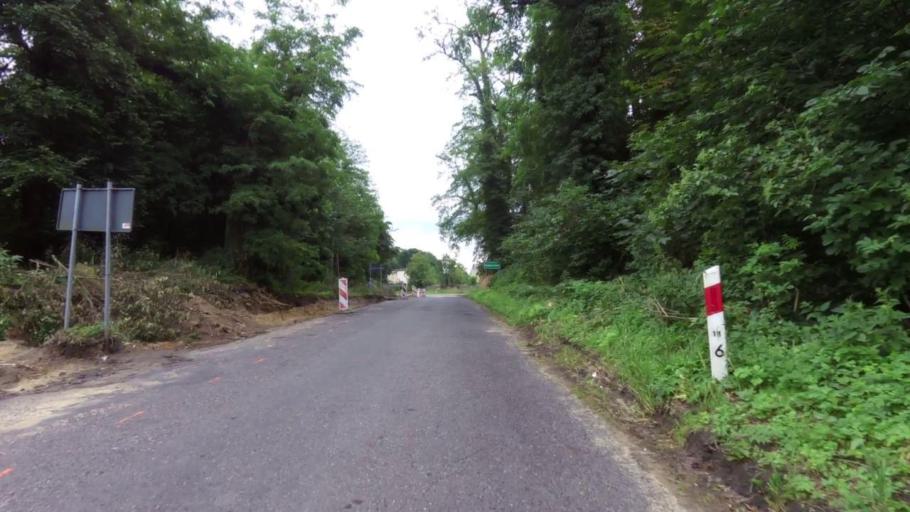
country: PL
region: West Pomeranian Voivodeship
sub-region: Powiat gryfinski
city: Cedynia
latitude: 52.8692
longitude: 14.2285
